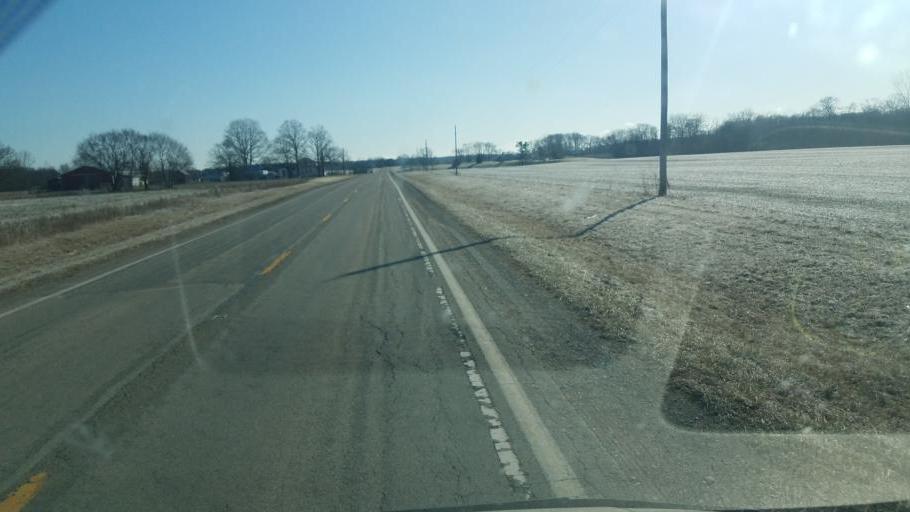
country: US
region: Ohio
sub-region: Morrow County
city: Cardington
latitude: 40.5172
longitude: -82.9378
